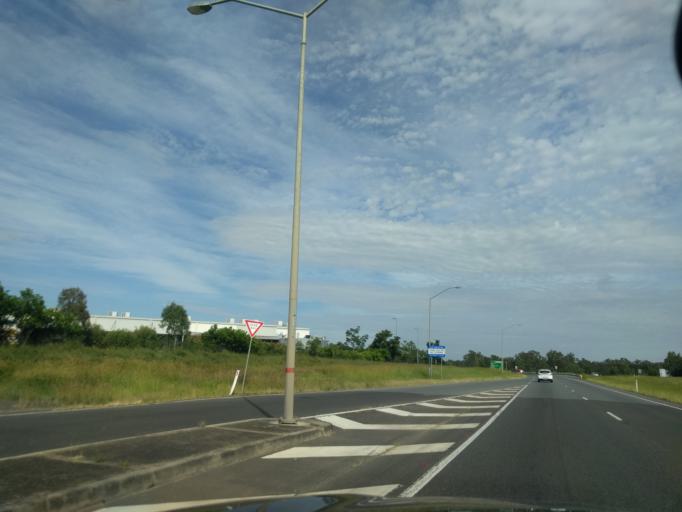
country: AU
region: Queensland
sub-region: Ipswich
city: Bundamba
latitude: -27.5850
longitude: 152.8186
